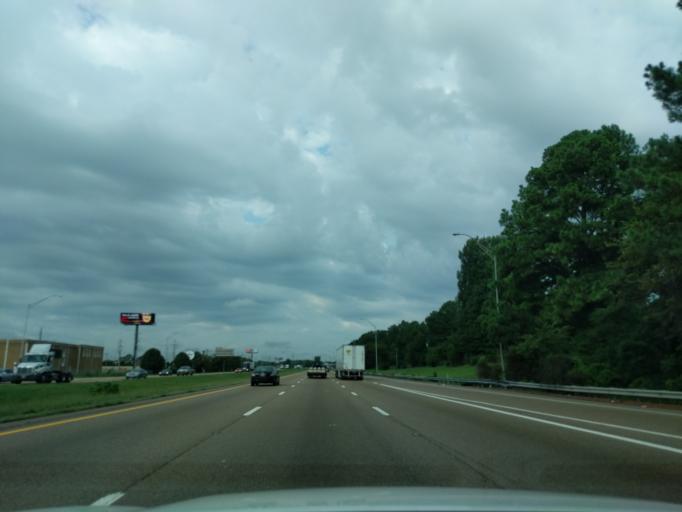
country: US
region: Tennessee
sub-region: Shelby County
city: New South Memphis
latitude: 35.0727
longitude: -90.0125
